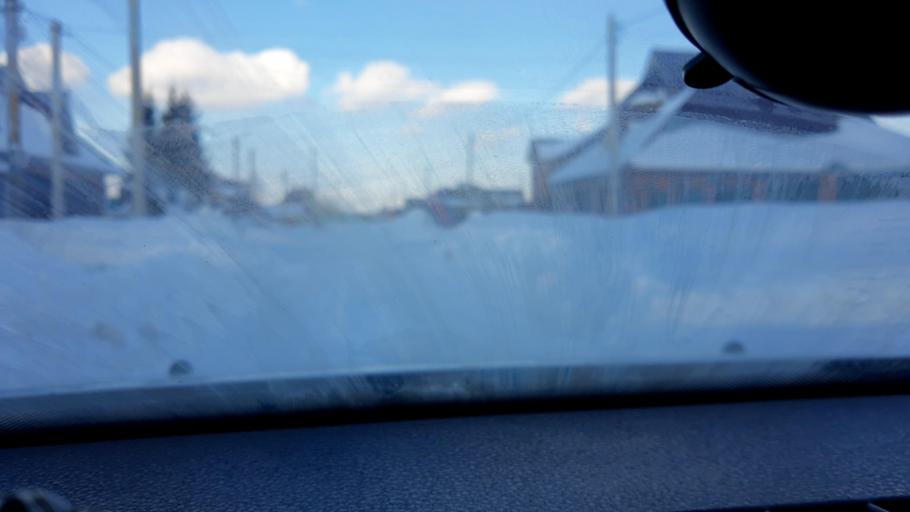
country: RU
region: Bashkortostan
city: Ufa
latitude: 54.6536
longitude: 56.0656
